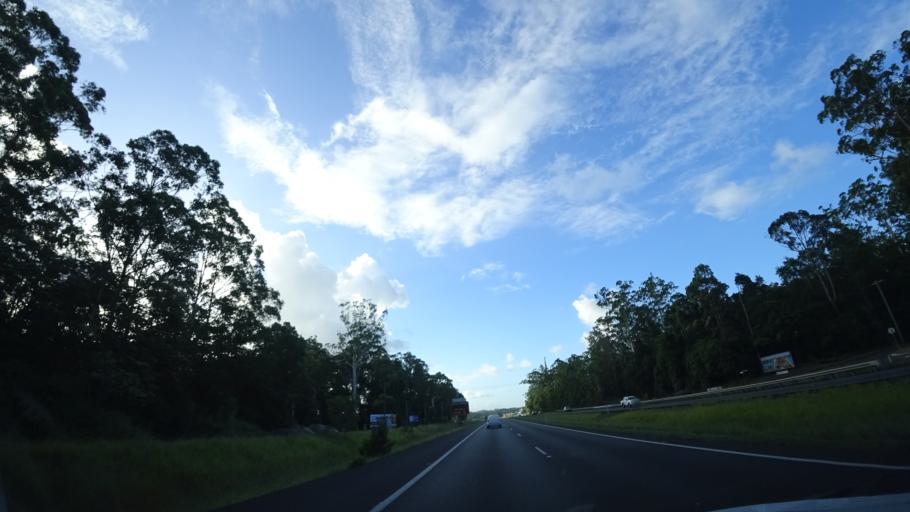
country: AU
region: Queensland
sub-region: Sunshine Coast
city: Buderim
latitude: -26.6972
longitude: 153.0114
